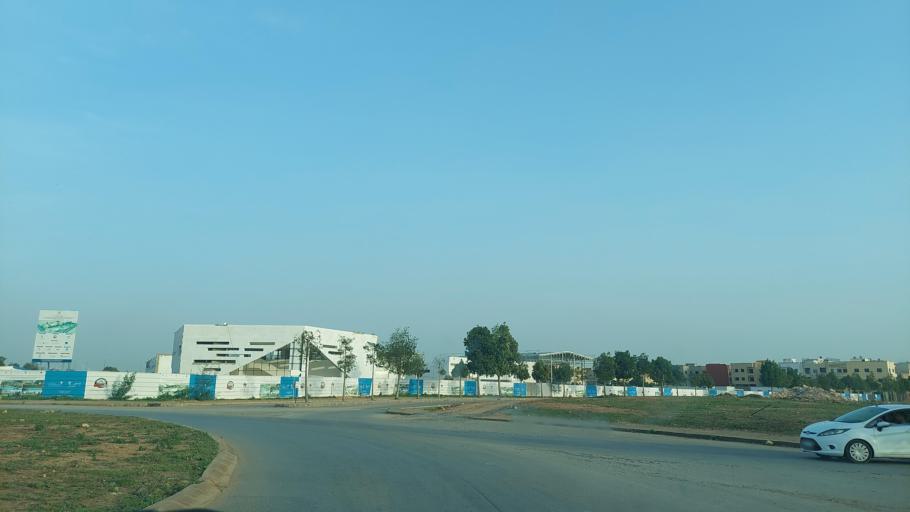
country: MA
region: Grand Casablanca
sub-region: Mediouna
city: Mediouna
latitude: 33.3919
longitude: -7.5473
